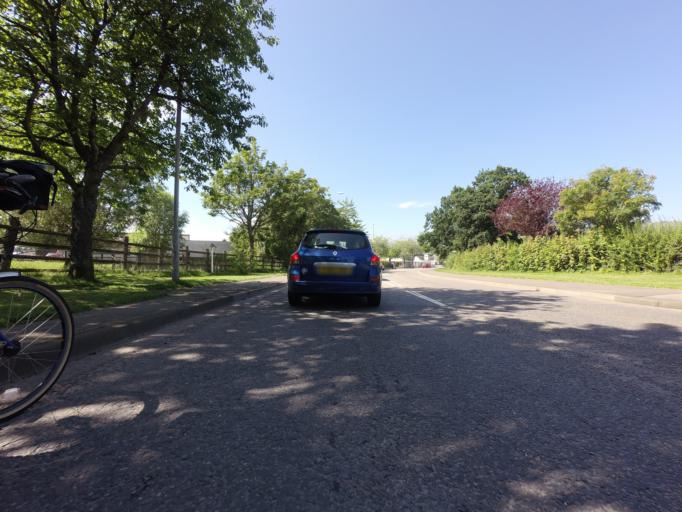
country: GB
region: Scotland
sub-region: Highland
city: Dingwall
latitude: 57.5941
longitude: -4.4303
